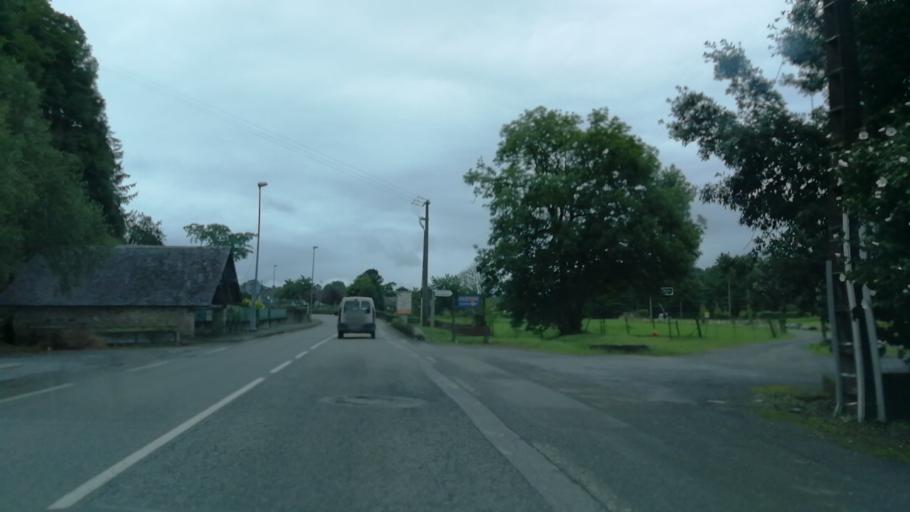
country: FR
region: Aquitaine
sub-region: Departement des Pyrenees-Atlantiques
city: Oloron-Sainte-Marie
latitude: 43.1173
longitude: -0.6147
